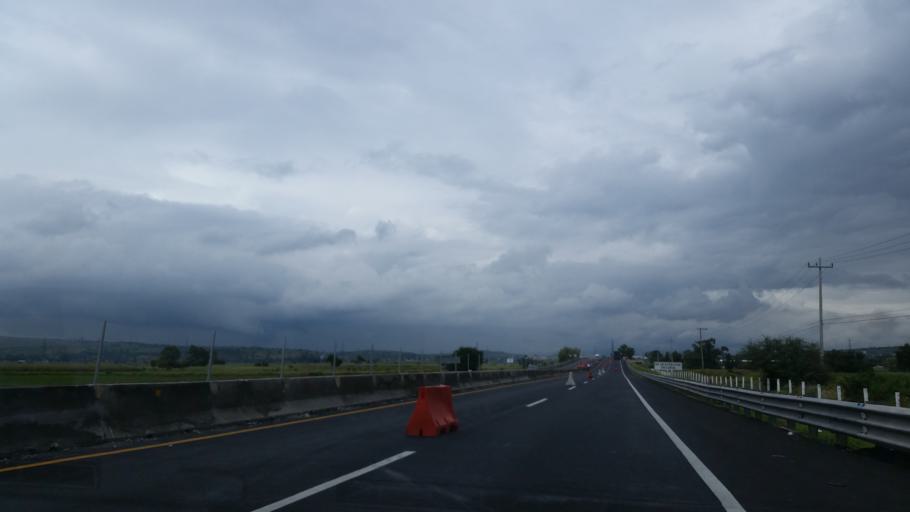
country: MX
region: Mexico
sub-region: Huehuetoca
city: Casa Nueva
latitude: 19.8224
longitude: -99.2125
